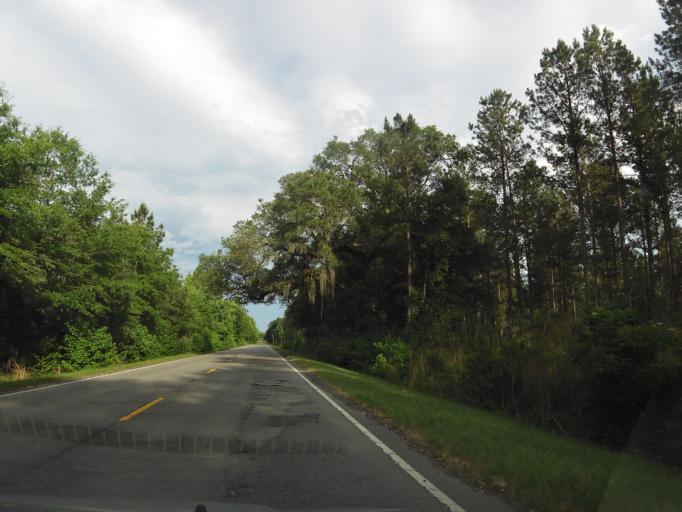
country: US
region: South Carolina
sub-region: Hampton County
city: Estill
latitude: 32.5955
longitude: -81.2151
